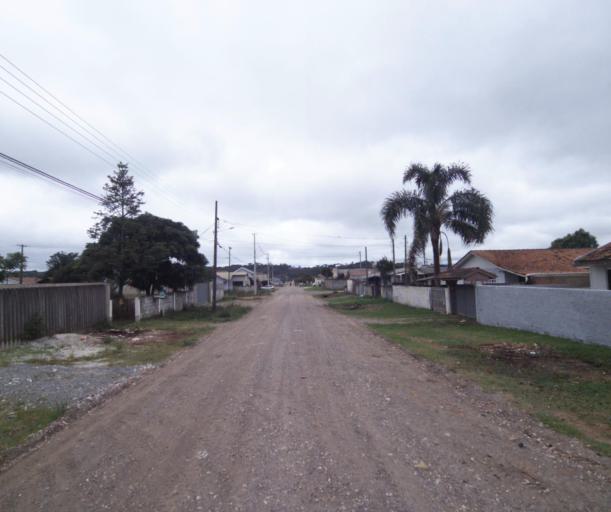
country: BR
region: Parana
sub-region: Quatro Barras
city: Quatro Barras
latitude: -25.3603
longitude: -49.0998
